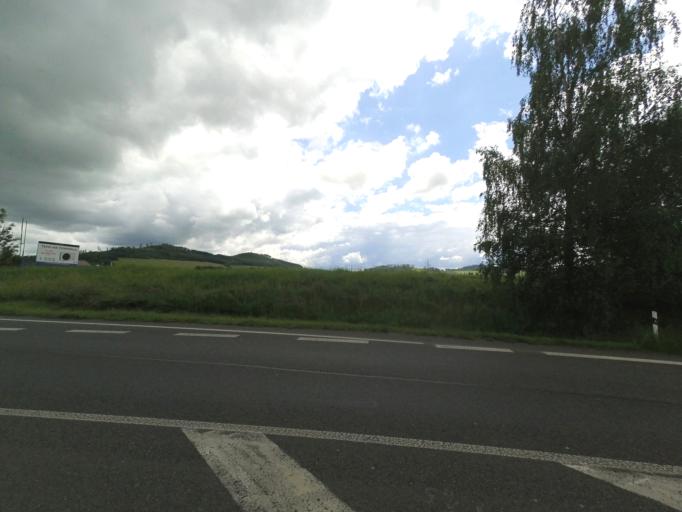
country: CZ
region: Plzensky
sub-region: Okres Domazlice
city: Kdyne
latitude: 49.3927
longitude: 13.0259
